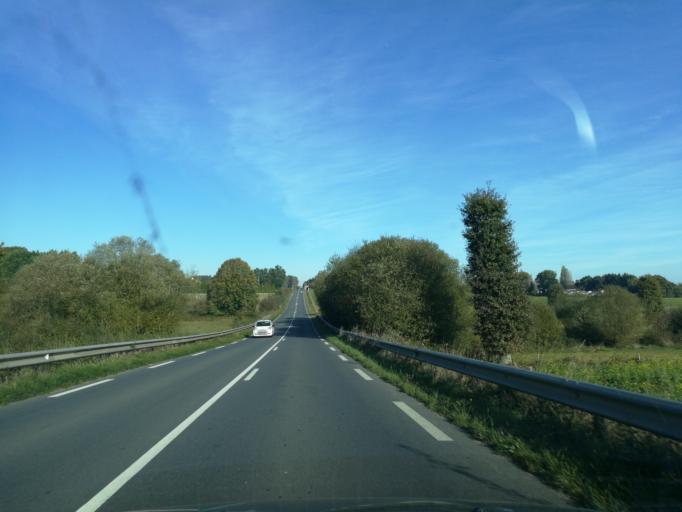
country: FR
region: Brittany
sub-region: Departement d'Ille-et-Vilaine
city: Bedee
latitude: 48.1637
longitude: -1.9456
